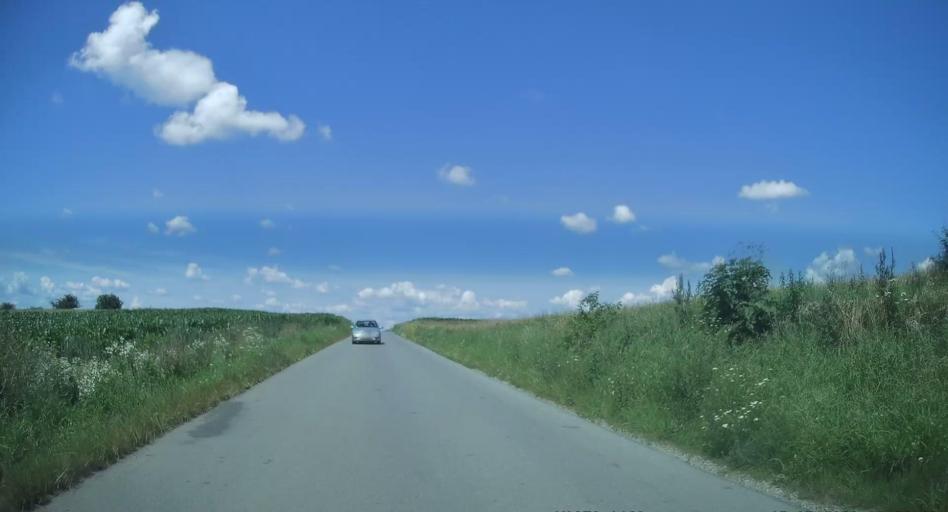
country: PL
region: Subcarpathian Voivodeship
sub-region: Powiat jaroslawski
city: Sosnica
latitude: 49.8485
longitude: 22.8870
